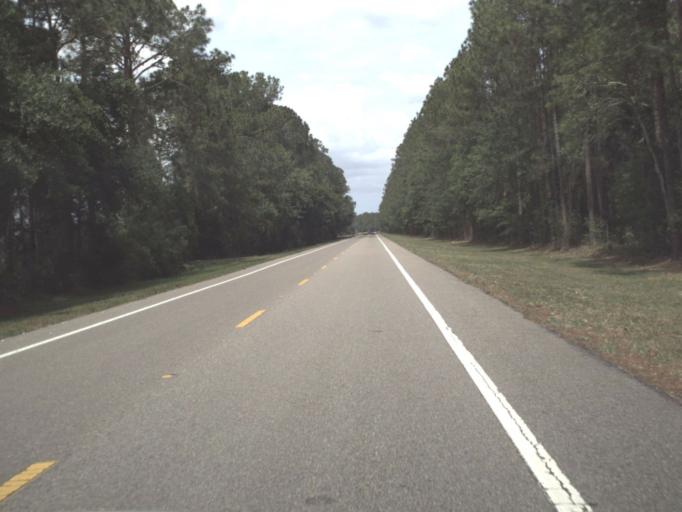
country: US
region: Florida
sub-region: Volusia County
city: Pierson
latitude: 29.3093
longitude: -81.3159
